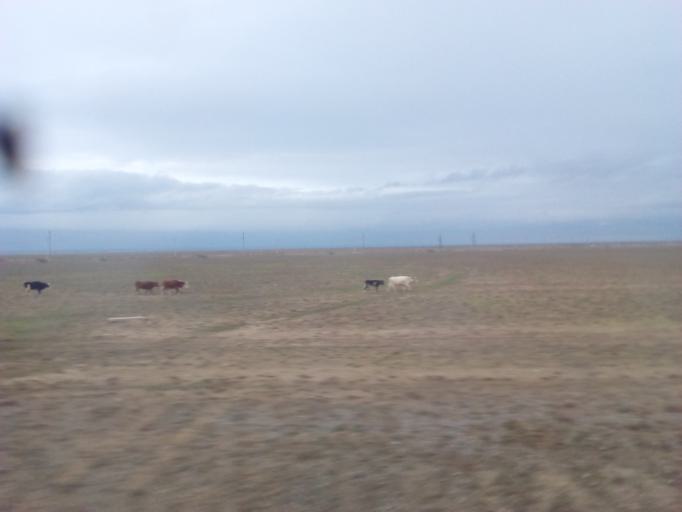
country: KZ
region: Ongtustik Qazaqstan
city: Sholaqqkorghan
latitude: 43.7902
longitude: 69.1483
